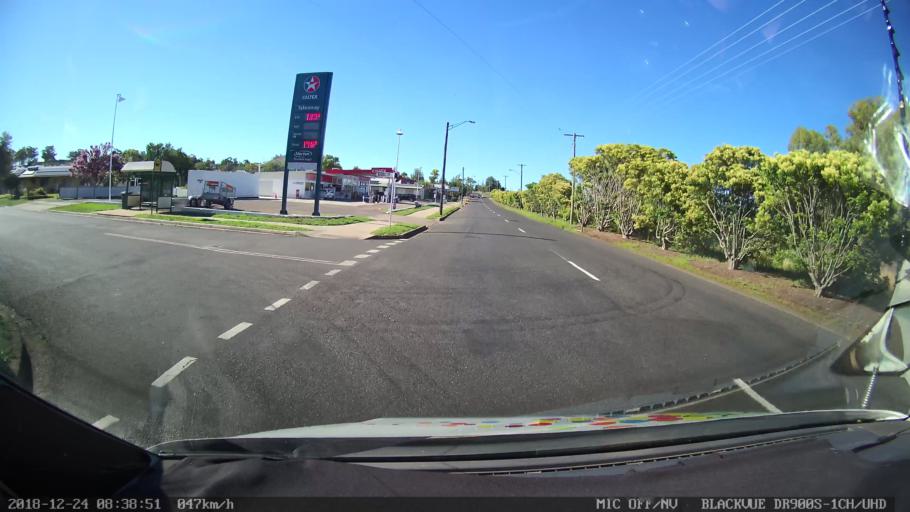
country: AU
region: New South Wales
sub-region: Liverpool Plains
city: Quirindi
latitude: -31.3439
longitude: 150.6475
